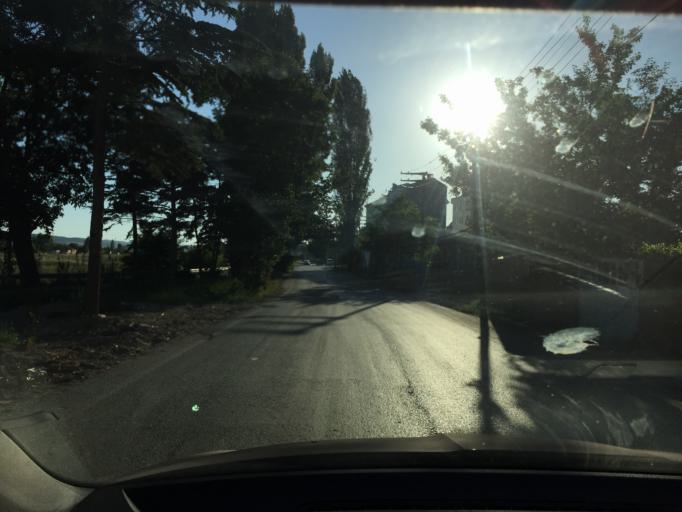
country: TR
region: Eskisehir
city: Eskisehir
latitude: 39.7749
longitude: 30.4578
